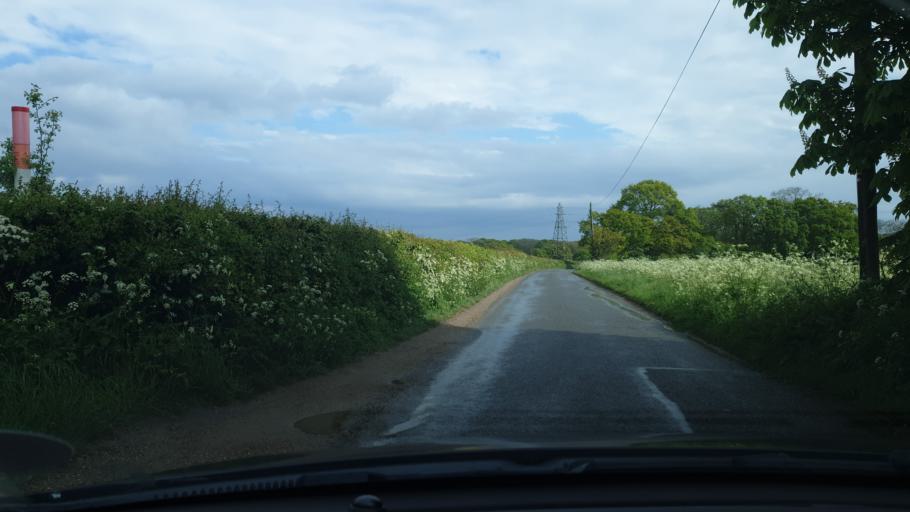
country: GB
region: England
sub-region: Essex
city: Great Bentley
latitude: 51.8447
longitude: 1.0495
